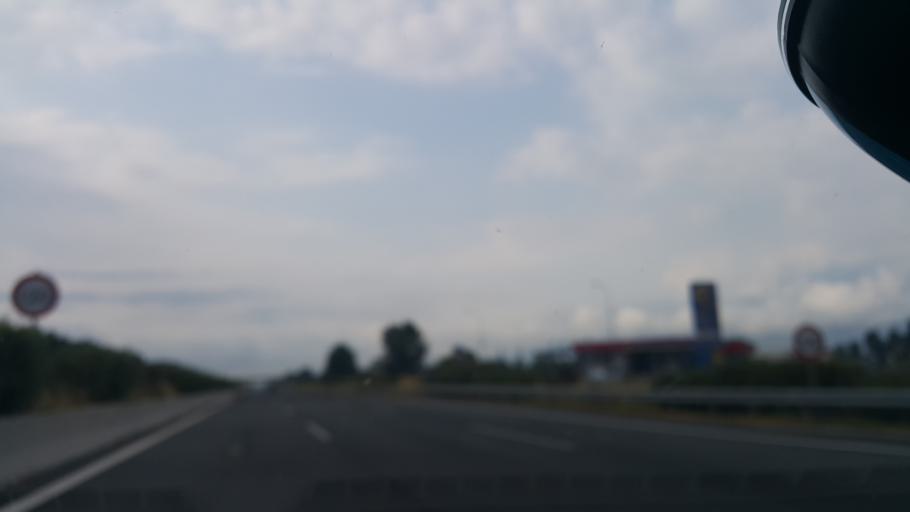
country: GR
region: Central Macedonia
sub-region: Nomos Pierias
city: Nea Efesos
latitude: 40.2321
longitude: 22.5382
